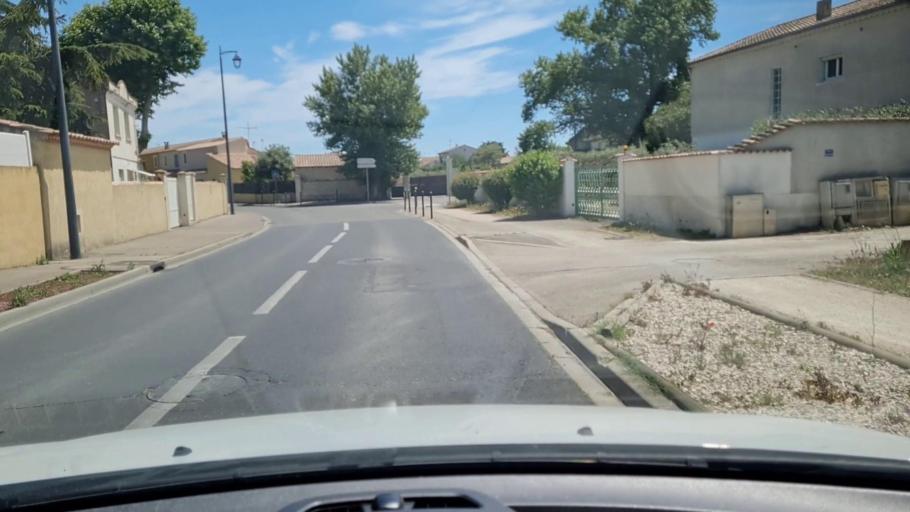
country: FR
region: Languedoc-Roussillon
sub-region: Departement du Gard
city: Aigues-Mortes
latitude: 43.5693
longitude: 4.1852
